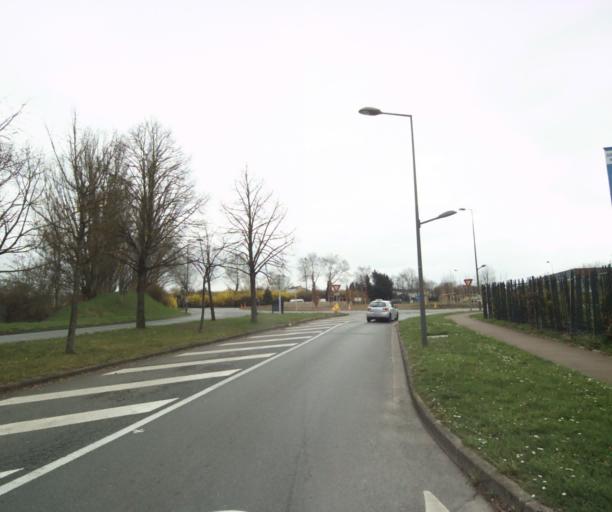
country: FR
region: Ile-de-France
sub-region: Departement du Val-d'Oise
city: Osny
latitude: 49.0527
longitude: 2.0465
